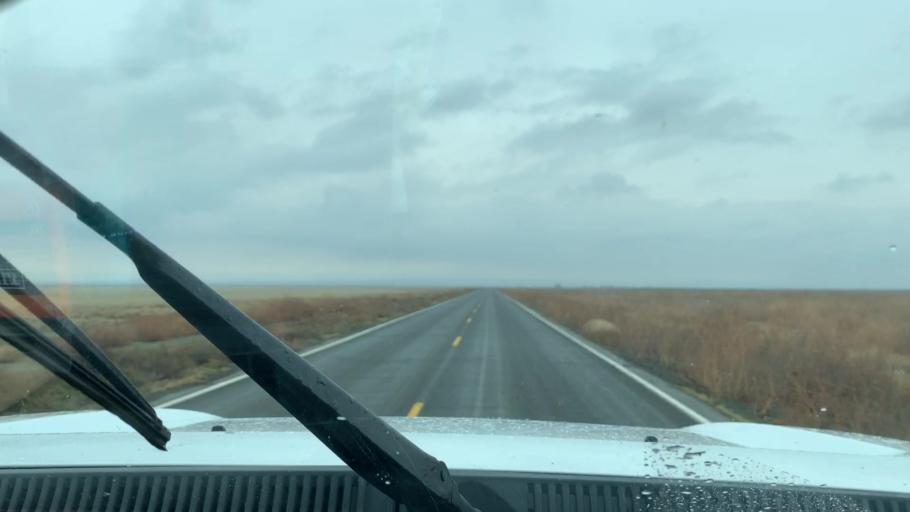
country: US
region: California
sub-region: Kings County
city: Kettleman City
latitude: 35.9341
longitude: -119.7726
